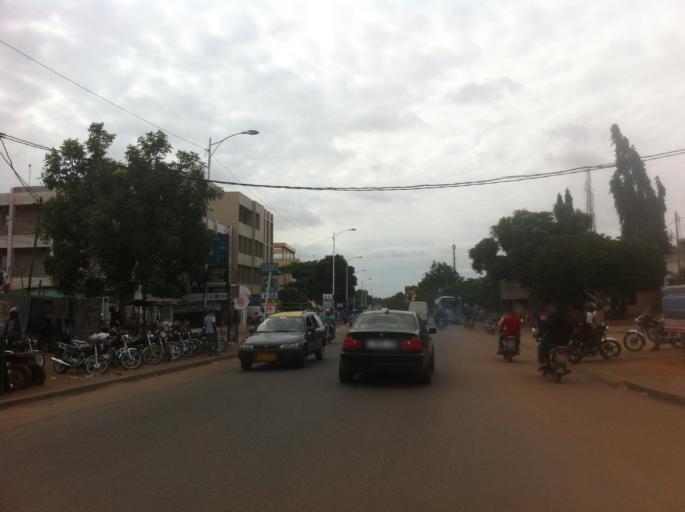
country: TG
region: Maritime
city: Lome
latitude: 6.1814
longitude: 1.1706
